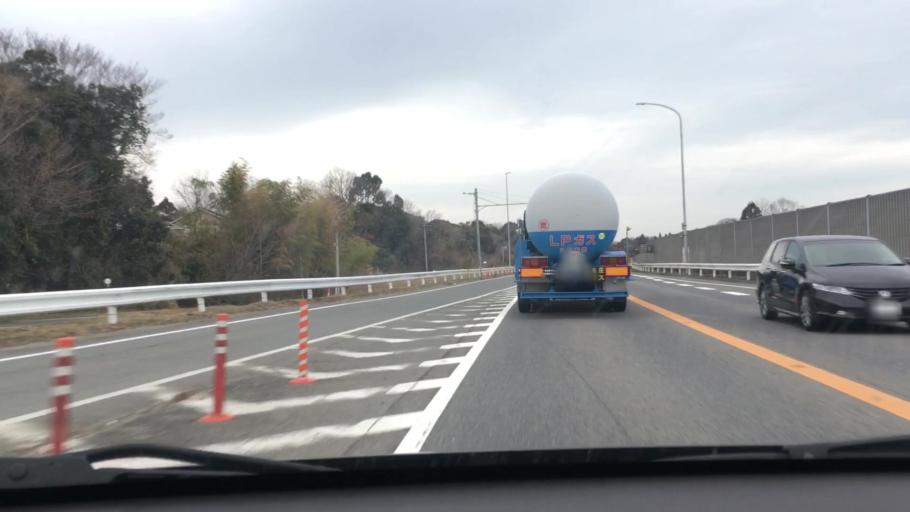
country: JP
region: Mie
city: Kameyama
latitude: 34.8647
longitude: 136.4433
